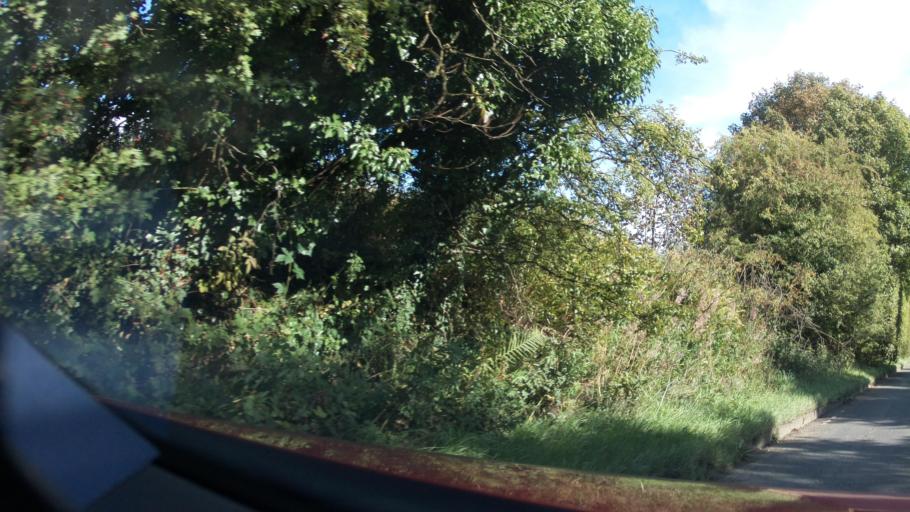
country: GB
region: Scotland
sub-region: Stirling
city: Cowie
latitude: 56.0558
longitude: -3.8672
